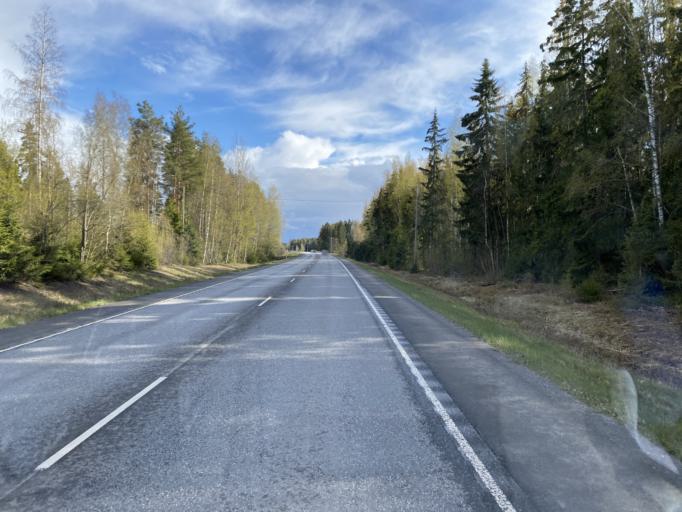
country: FI
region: Pirkanmaa
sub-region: Tampere
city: Lempaeaelae
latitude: 61.2843
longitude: 23.7435
